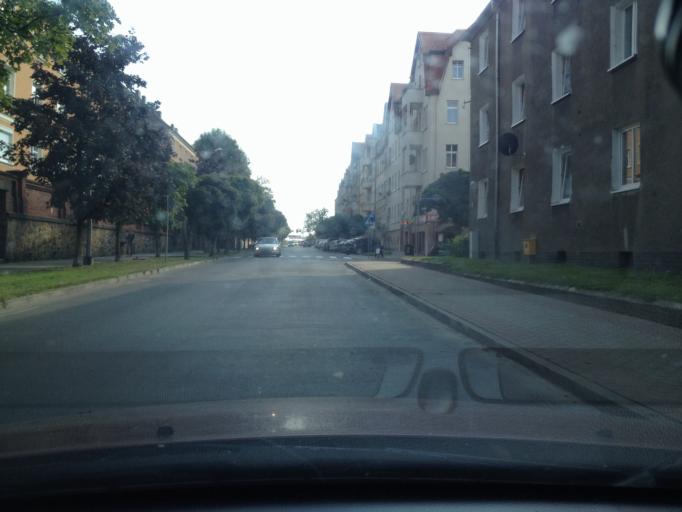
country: PL
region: Lower Silesian Voivodeship
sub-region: Powiat zgorzelecki
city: Zgorzelec
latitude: 51.1516
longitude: 15.0098
